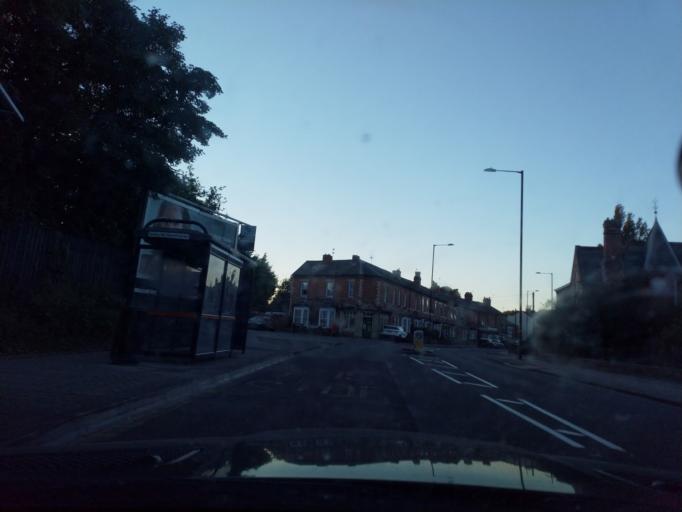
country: GB
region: England
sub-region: City and Borough of Birmingham
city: Acocks Green
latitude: 52.4563
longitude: -1.8192
